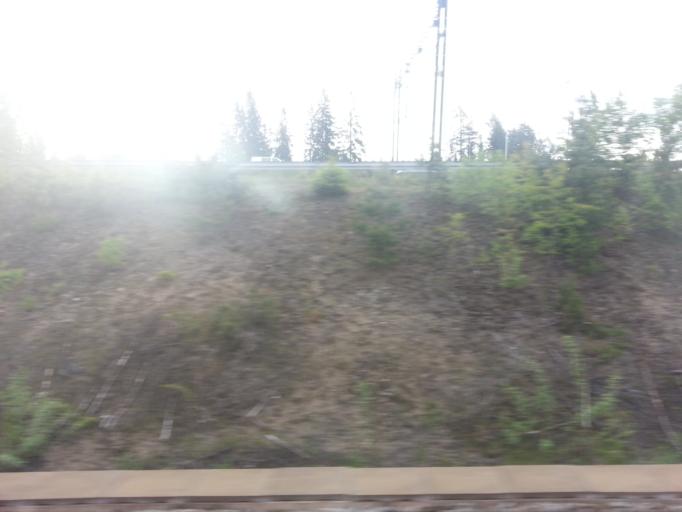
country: NO
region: Akershus
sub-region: Nannestad
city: Teigebyen
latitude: 60.1829
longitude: 11.0917
